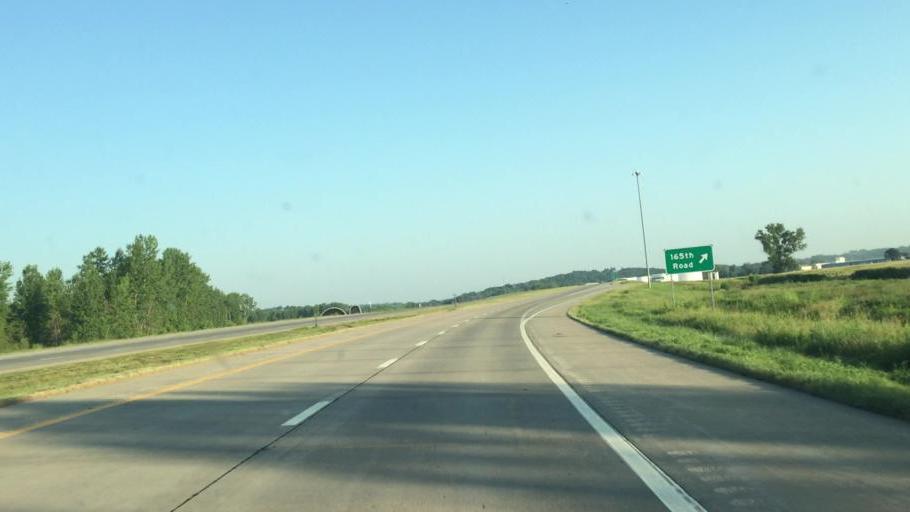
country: US
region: Kansas
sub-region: Doniphan County
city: Wathena
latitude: 39.7431
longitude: -94.9202
